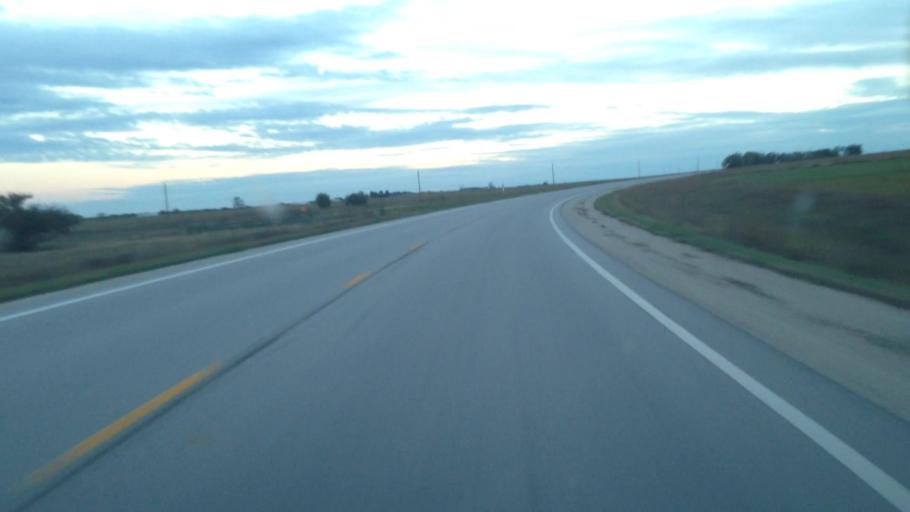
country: US
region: Kansas
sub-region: Anderson County
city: Garnett
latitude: 38.1924
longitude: -95.2423
